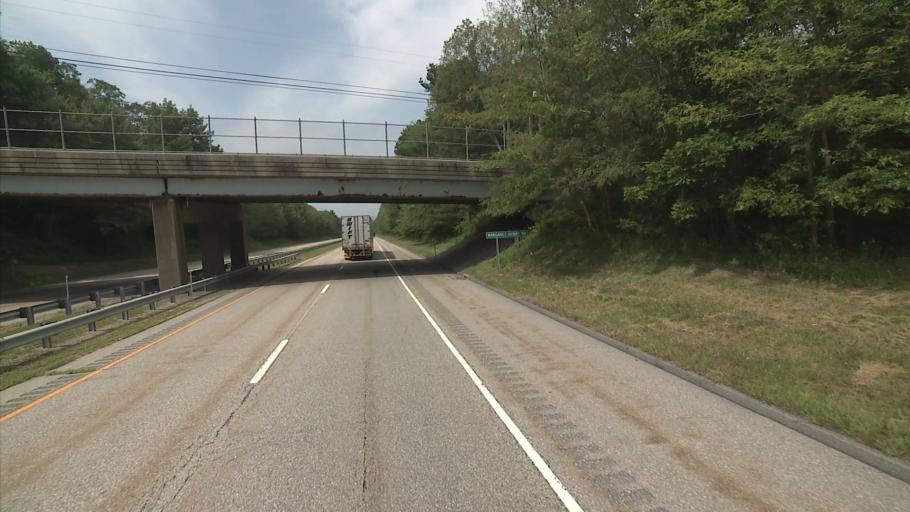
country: US
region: Connecticut
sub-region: Windham County
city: Danielson
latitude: 41.7827
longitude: -71.8253
